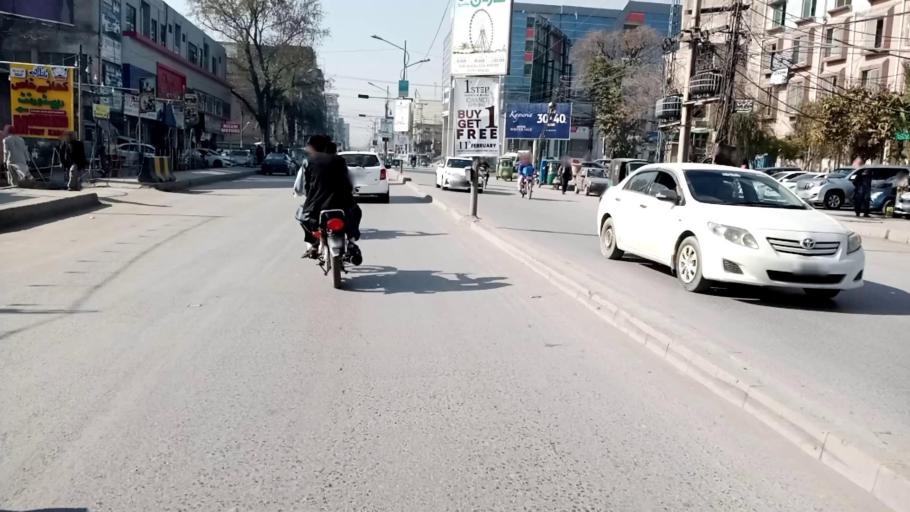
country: PK
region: Khyber Pakhtunkhwa
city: Peshawar
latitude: 34.0009
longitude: 71.5434
